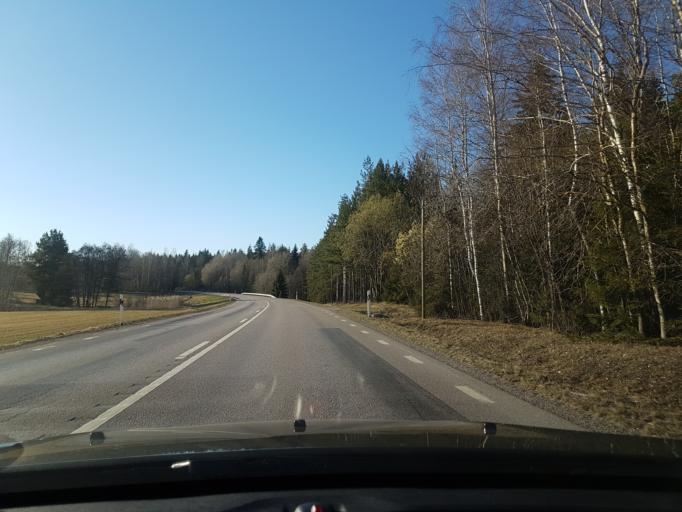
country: SE
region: Uppsala
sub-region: Heby Kommun
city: Morgongava
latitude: 59.9153
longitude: 17.0258
